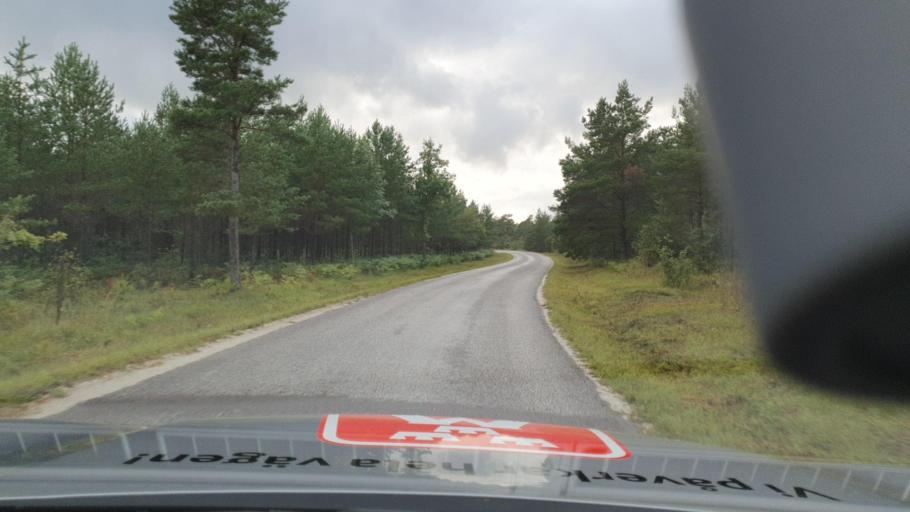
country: SE
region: Gotland
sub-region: Gotland
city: Vibble
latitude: 57.5478
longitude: 18.2471
